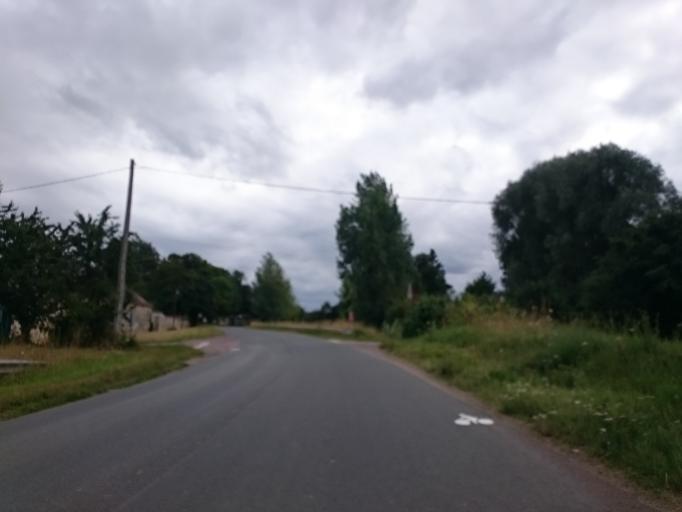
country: FR
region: Lower Normandy
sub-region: Departement du Calvados
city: Louvigny
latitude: 49.1383
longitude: -0.3947
